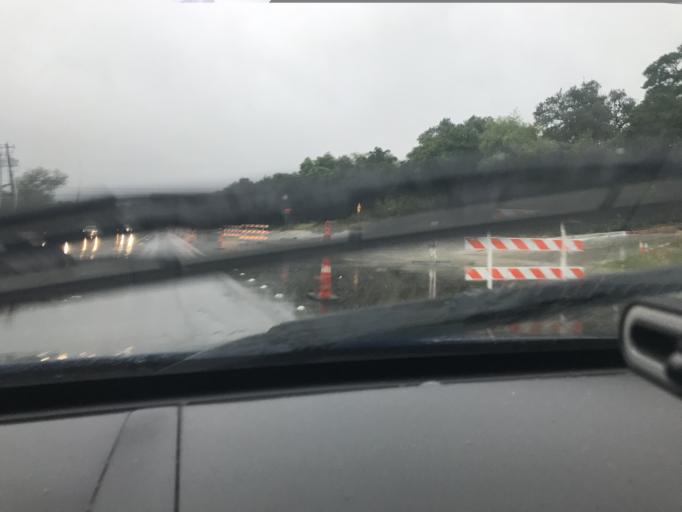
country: US
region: Texas
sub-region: Travis County
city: West Lake Hills
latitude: 30.2902
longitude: -97.8197
